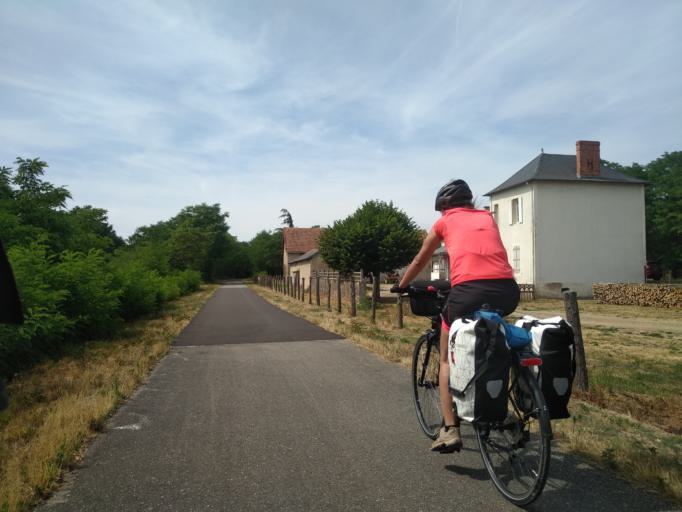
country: FR
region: Auvergne
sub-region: Departement de l'Allier
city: Diou
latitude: 46.5416
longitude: 3.7484
